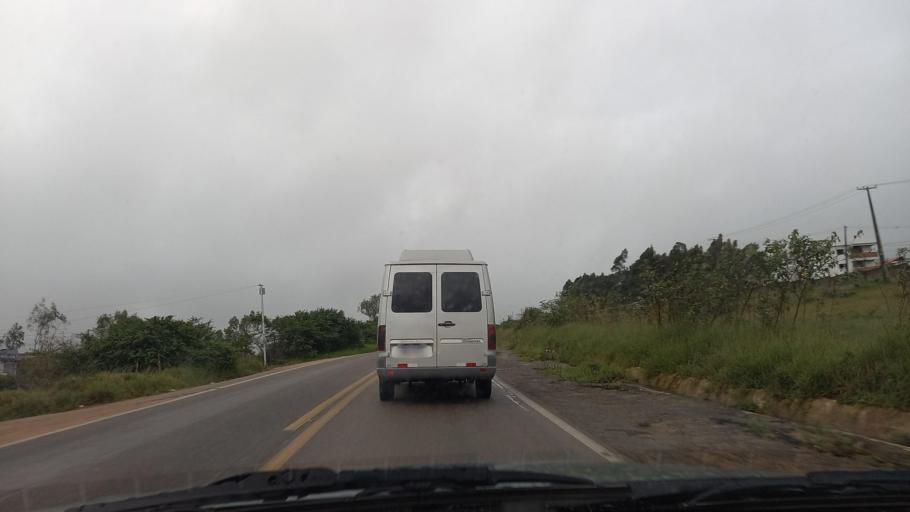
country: BR
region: Pernambuco
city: Garanhuns
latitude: -8.8680
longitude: -36.5086
